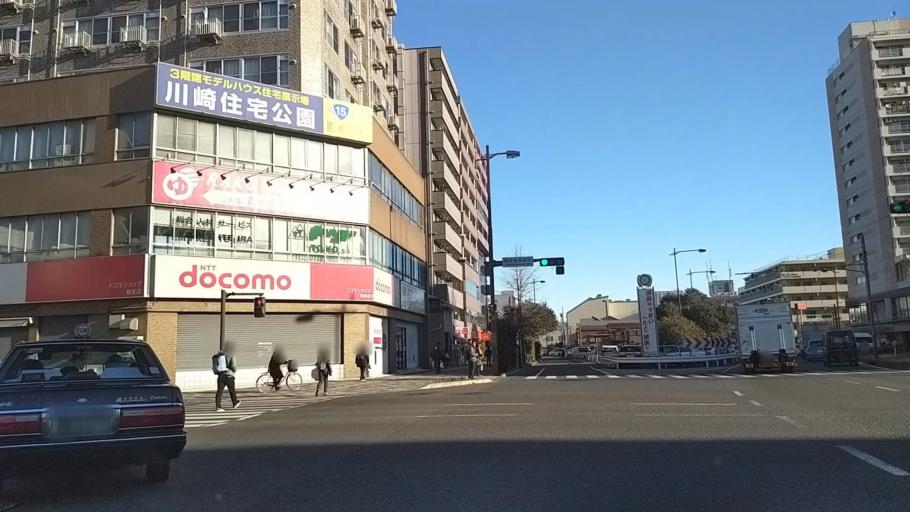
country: JP
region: Kanagawa
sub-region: Kawasaki-shi
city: Kawasaki
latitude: 35.5086
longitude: 139.6814
